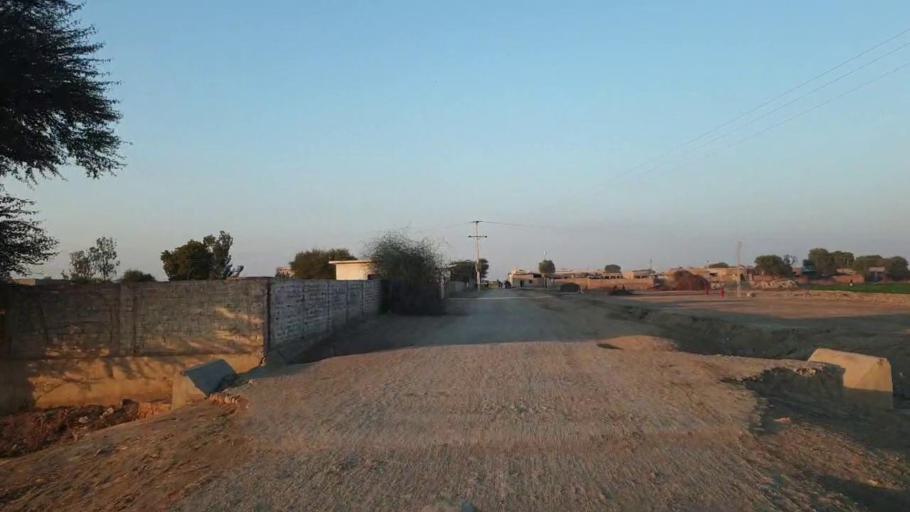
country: PK
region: Sindh
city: Shahpur Chakar
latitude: 26.1589
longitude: 68.5422
